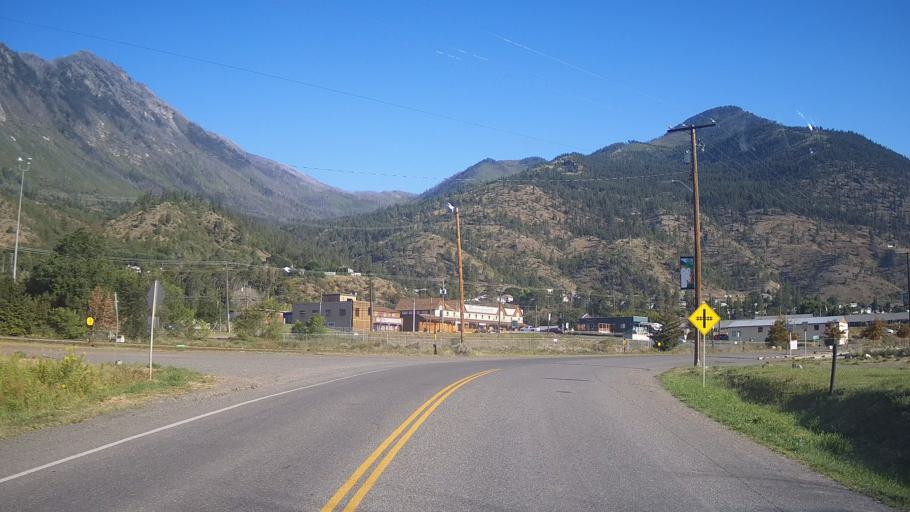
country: CA
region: British Columbia
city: Lillooet
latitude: 50.6846
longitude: -121.9348
